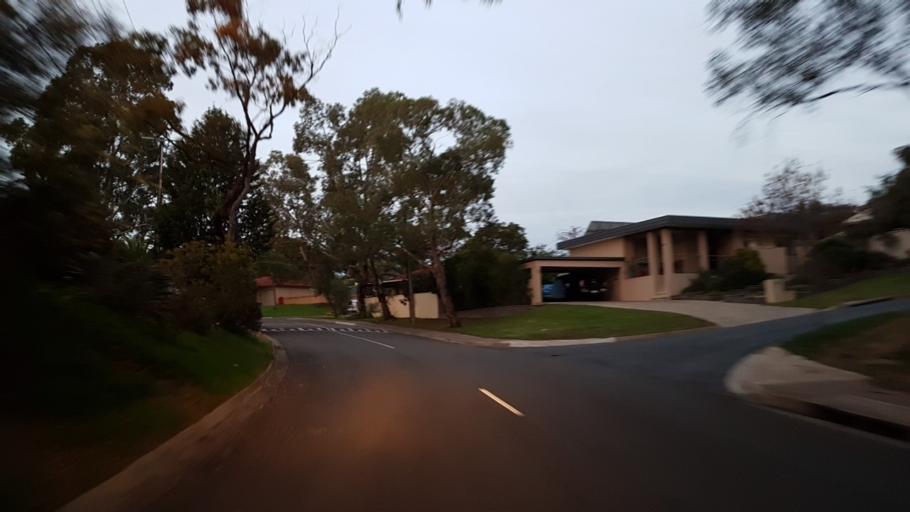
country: AU
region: South Australia
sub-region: Port Adelaide Enfield
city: Gilles Plains
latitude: -34.8398
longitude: 138.6593
